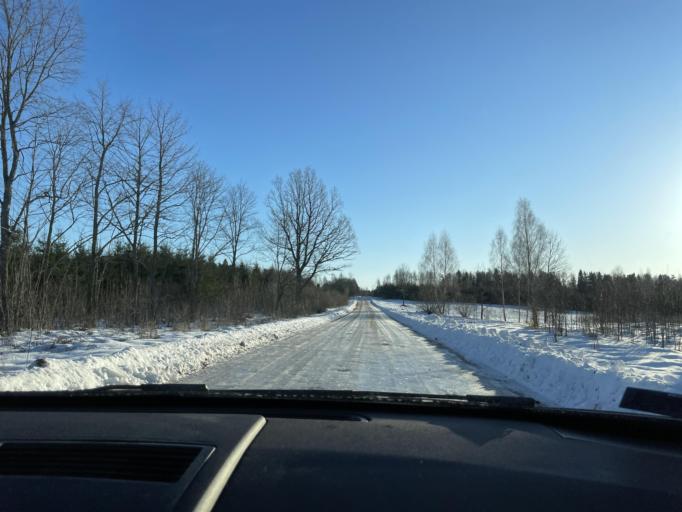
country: LV
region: Ludzas Rajons
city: Ludza
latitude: 56.4655
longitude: 27.6028
